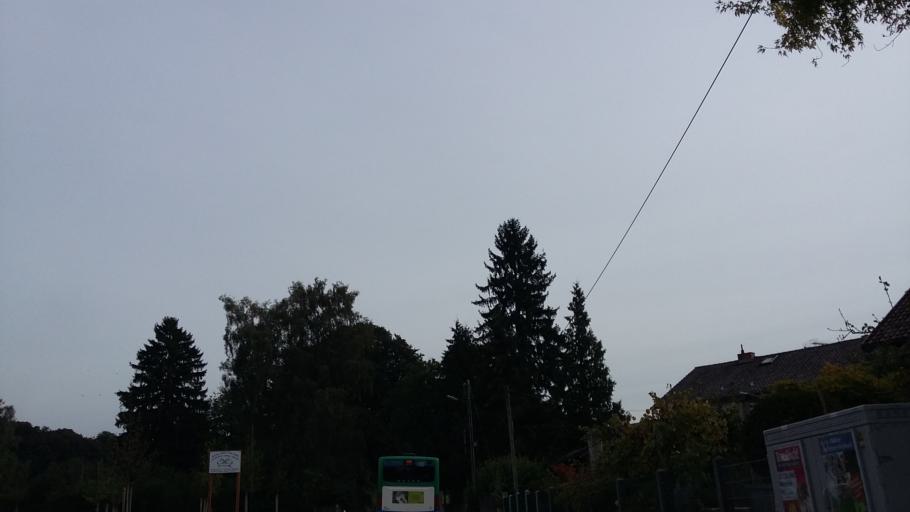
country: DE
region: Bavaria
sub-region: Upper Bavaria
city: Berg
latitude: 47.9638
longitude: 11.3580
